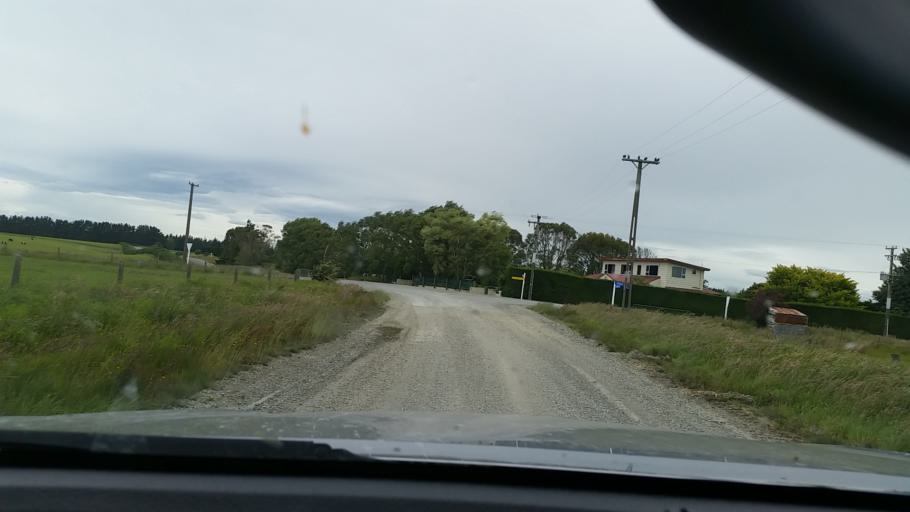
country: NZ
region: Southland
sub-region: Southland District
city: Winton
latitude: -46.2250
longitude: 168.5551
